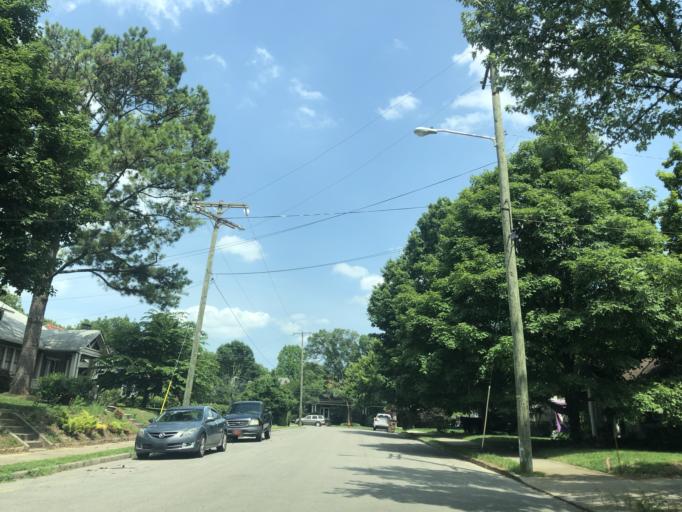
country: US
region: Tennessee
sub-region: Davidson County
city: Nashville
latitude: 36.1820
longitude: -86.7422
